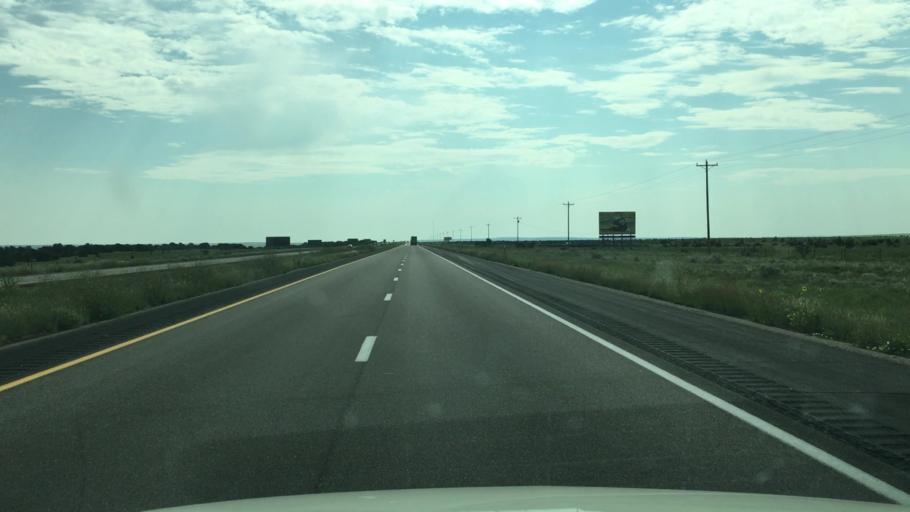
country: US
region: New Mexico
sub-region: San Miguel County
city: Las Vegas
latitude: 34.9937
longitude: -105.3414
